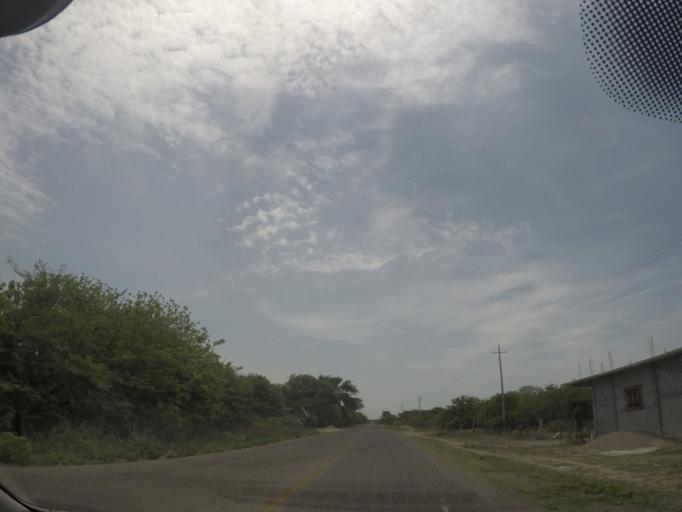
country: MX
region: Oaxaca
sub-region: San Mateo del Mar
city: Colonia Juarez
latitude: 16.2073
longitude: -95.0116
